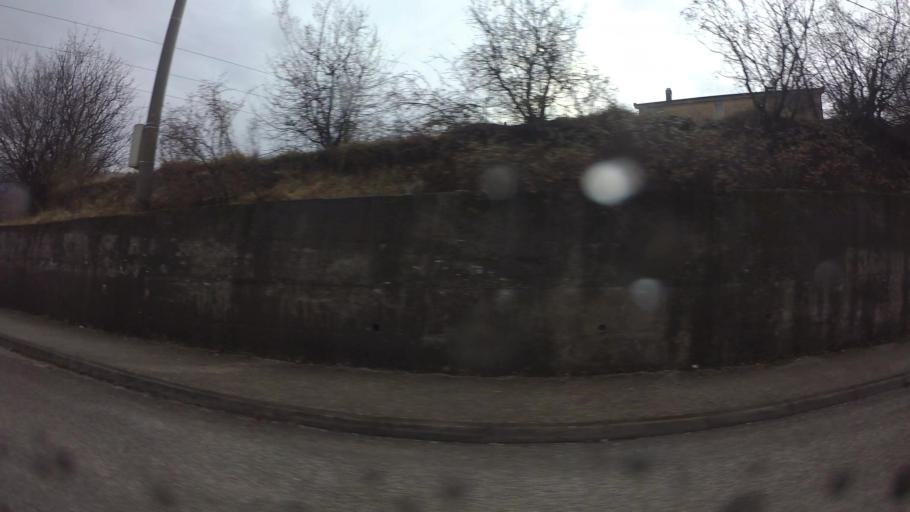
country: BA
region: Federation of Bosnia and Herzegovina
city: Cim
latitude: 43.3526
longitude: 17.7780
